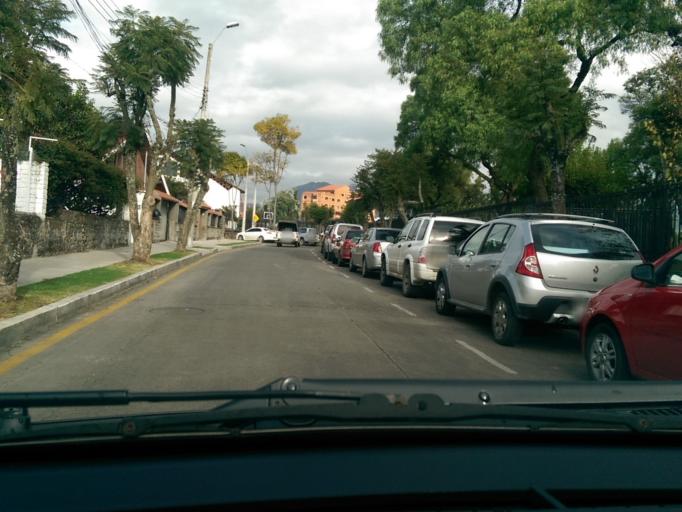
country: EC
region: Azuay
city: Cuenca
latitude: -2.9022
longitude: -79.0098
